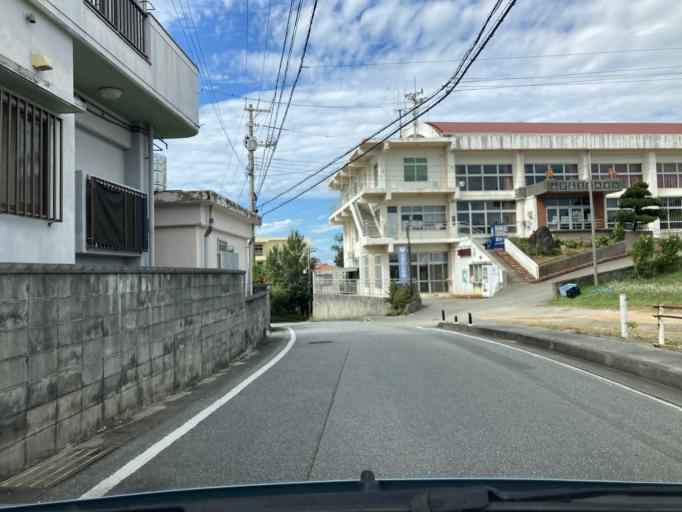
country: JP
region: Okinawa
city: Ishikawa
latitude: 26.4326
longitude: 127.7784
